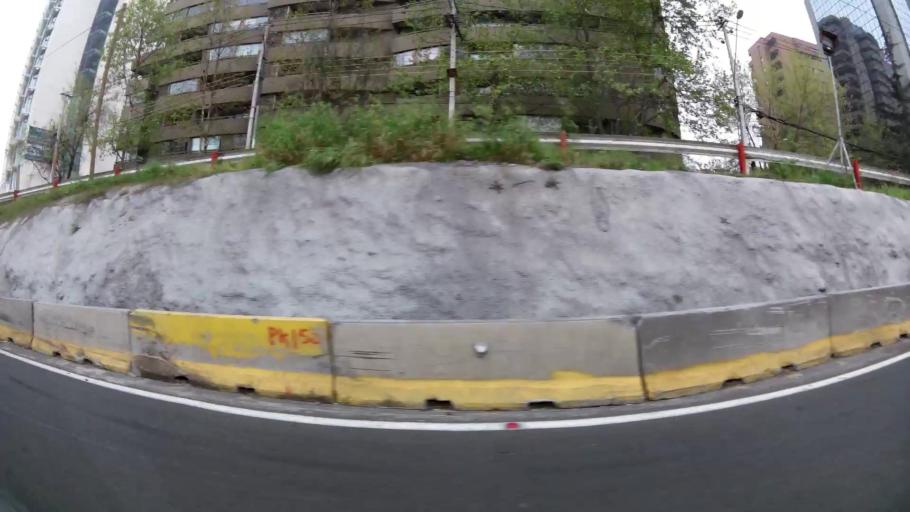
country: CL
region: Santiago Metropolitan
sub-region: Provincia de Santiago
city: Villa Presidente Frei, Nunoa, Santiago, Chile
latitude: -33.4035
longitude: -70.5852
